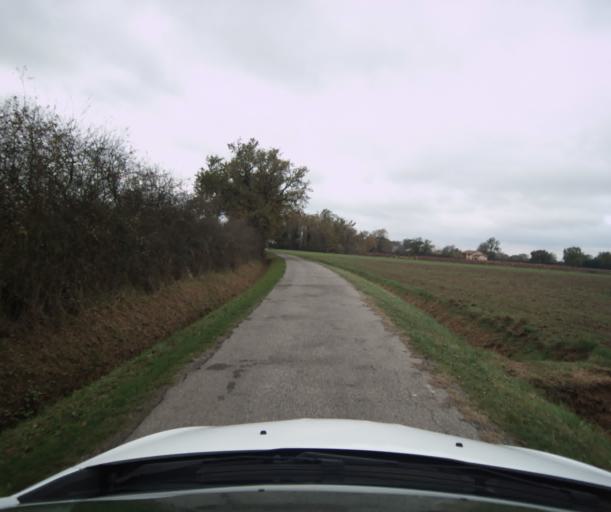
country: FR
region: Midi-Pyrenees
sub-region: Departement du Tarn-et-Garonne
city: Saint-Porquier
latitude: 44.0501
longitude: 1.1654
